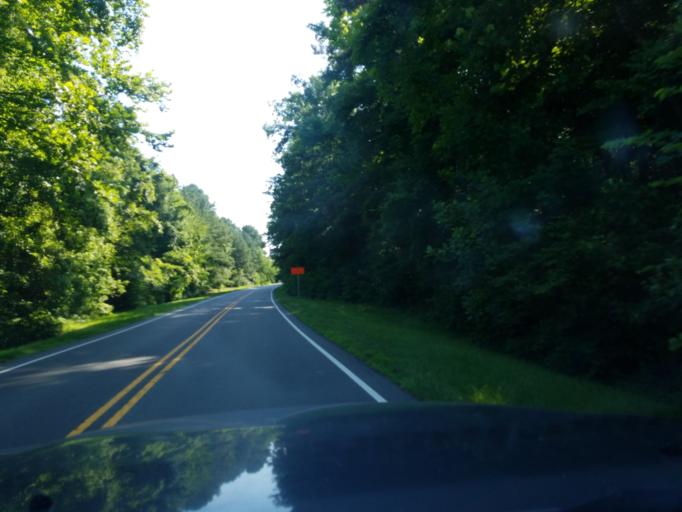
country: US
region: North Carolina
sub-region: Granville County
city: Oxford
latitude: 36.2457
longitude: -78.6917
